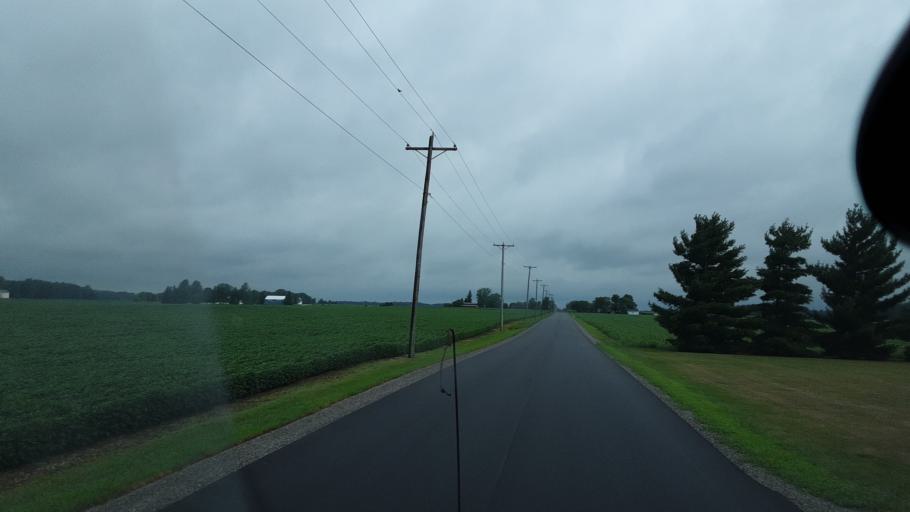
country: US
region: Indiana
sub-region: Adams County
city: Decatur
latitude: 40.8500
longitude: -84.8427
